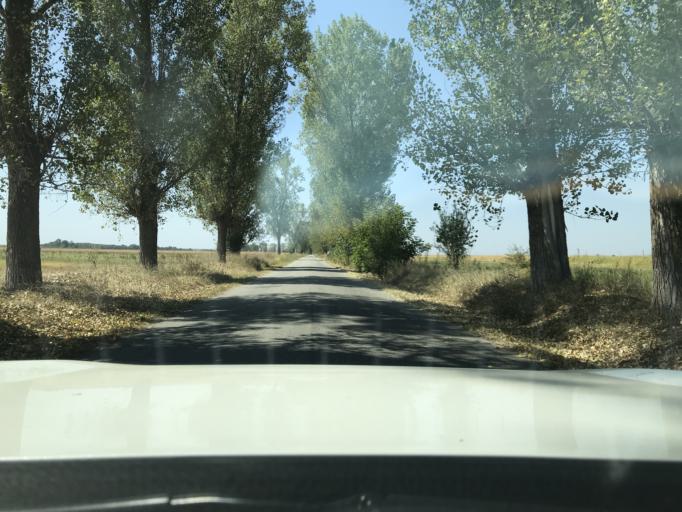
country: RO
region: Olt
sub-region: Comuna Falcoiu
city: Falcoiu
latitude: 44.2366
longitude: 24.3569
